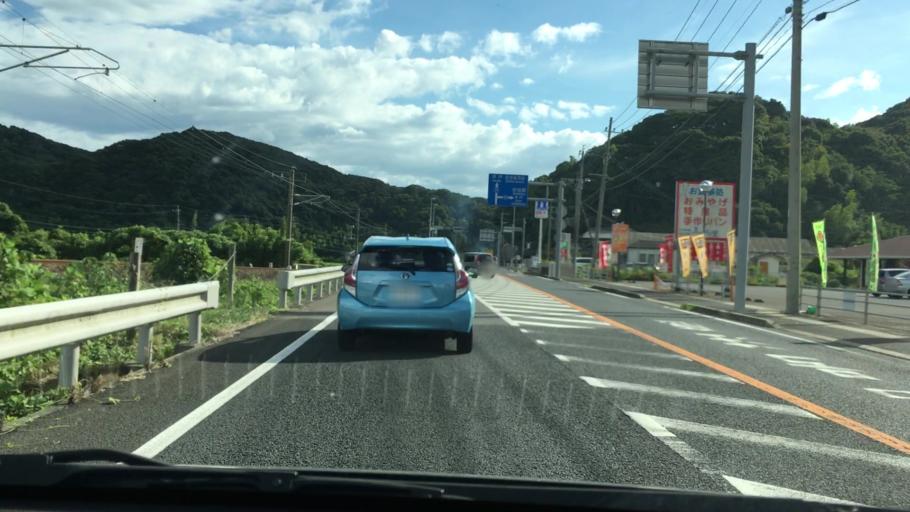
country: JP
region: Saga Prefecture
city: Imaricho-ko
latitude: 33.1677
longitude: 129.8417
